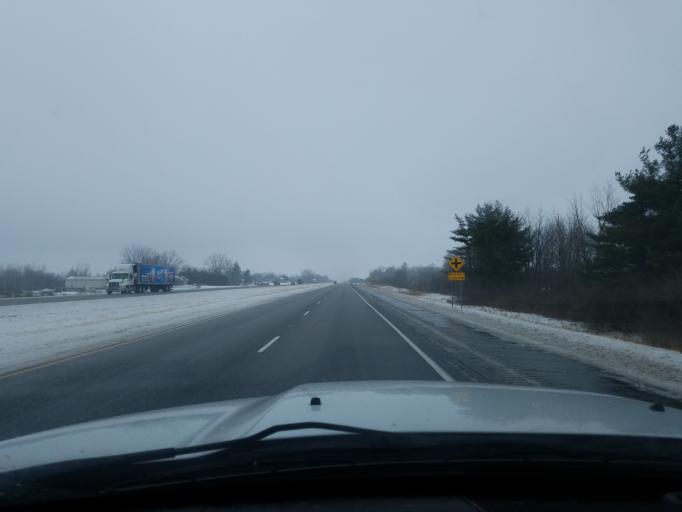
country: US
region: Indiana
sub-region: Fulton County
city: Rochester
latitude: 40.9560
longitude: -86.1682
